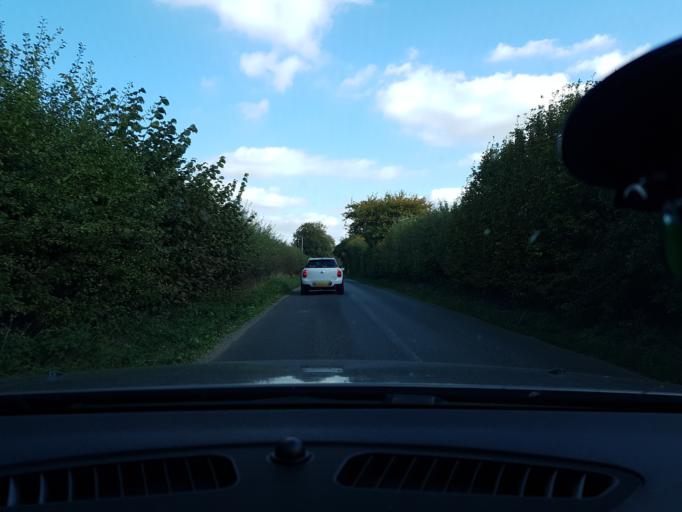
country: GB
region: England
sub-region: Wiltshire
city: Aldbourne
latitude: 51.5020
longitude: -1.6011
